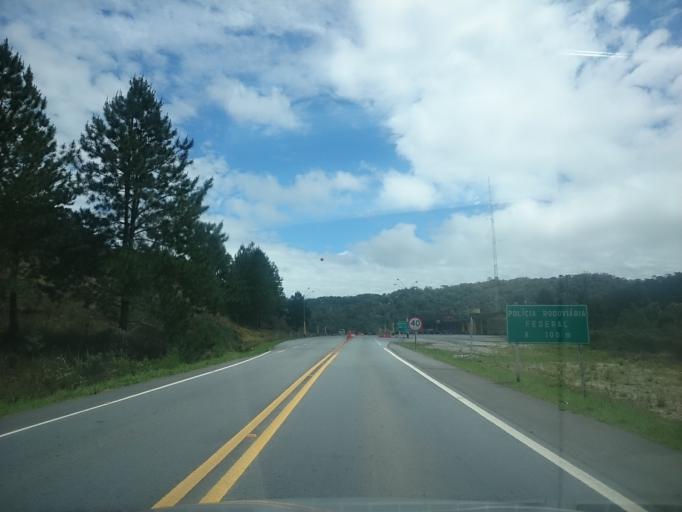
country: BR
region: Santa Catarina
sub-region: Anitapolis
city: Anitapolis
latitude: -27.6863
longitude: -49.0332
